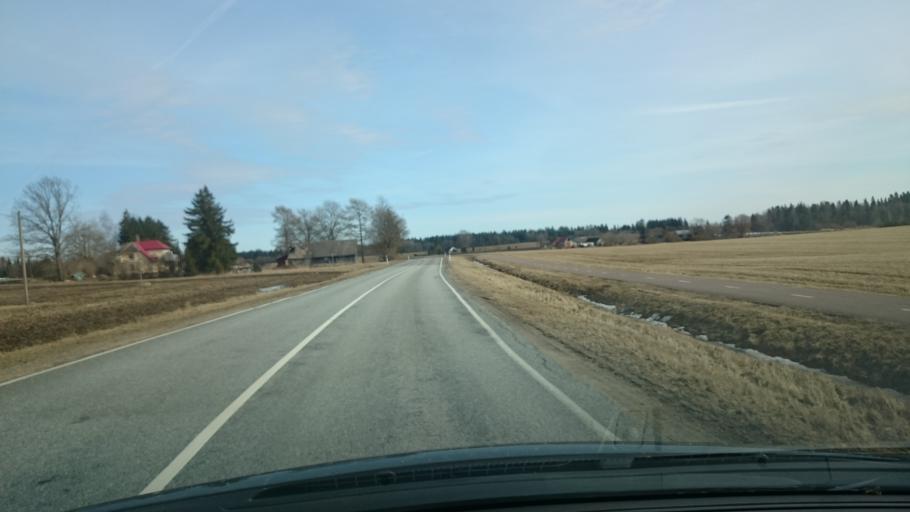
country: EE
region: Jaervamaa
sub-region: Tueri vald
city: Tueri
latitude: 58.8881
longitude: 25.4669
